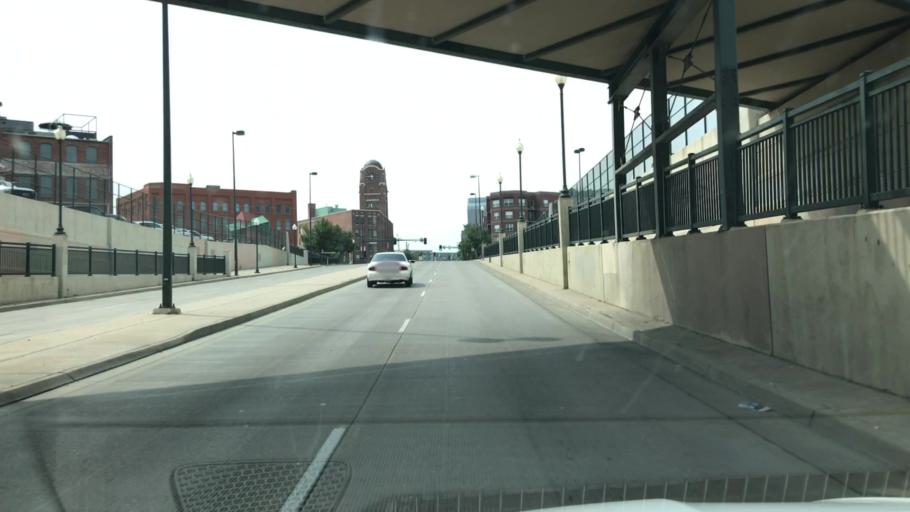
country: US
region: Colorado
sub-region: Denver County
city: Denver
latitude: 39.7611
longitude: -104.9880
